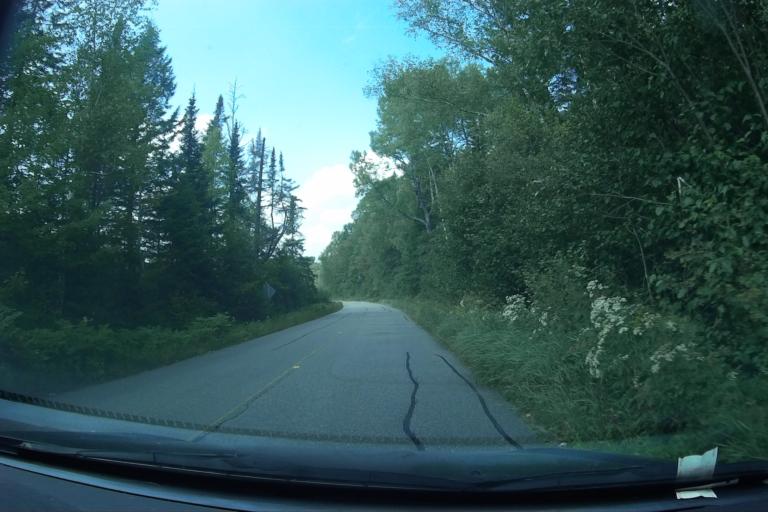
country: CA
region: Ontario
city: Bancroft
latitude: 45.5999
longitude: -78.3309
